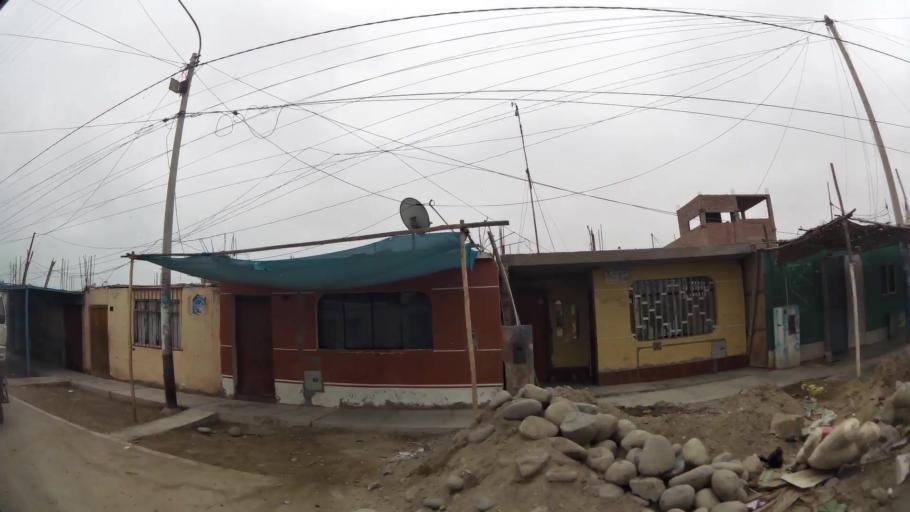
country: PE
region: Ica
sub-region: Provincia de Pisco
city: Pisco
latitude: -13.7339
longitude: -76.2174
